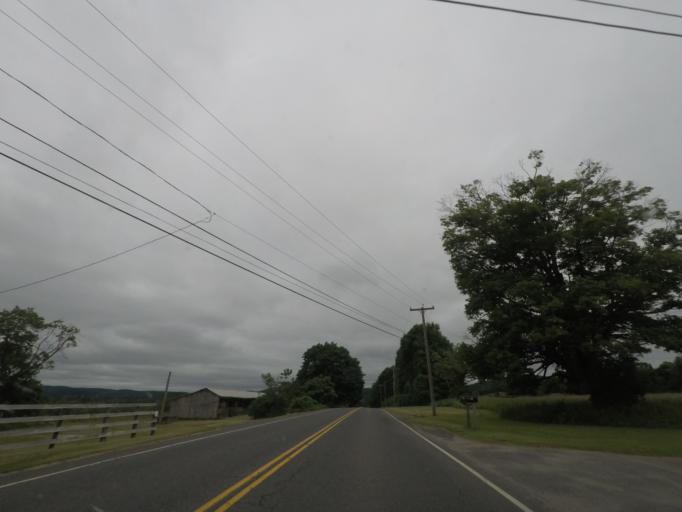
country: US
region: Connecticut
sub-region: Litchfield County
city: Canaan
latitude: 41.9340
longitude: -73.4265
